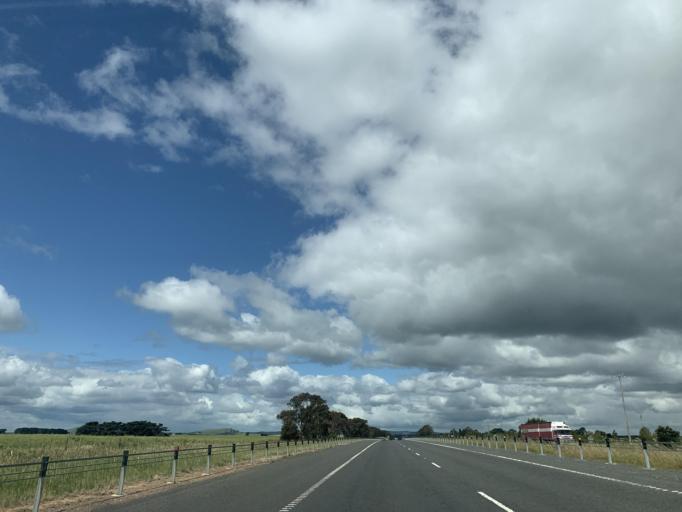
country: AU
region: Victoria
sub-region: Ballarat North
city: Newington
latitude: -37.4775
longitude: 143.6982
